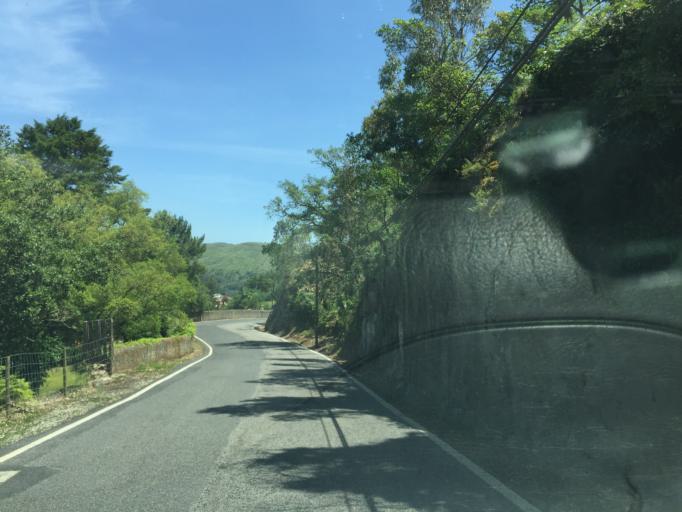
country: PT
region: Lisbon
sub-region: Mafra
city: Venda do Pinheiro
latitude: 38.8903
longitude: -9.2164
